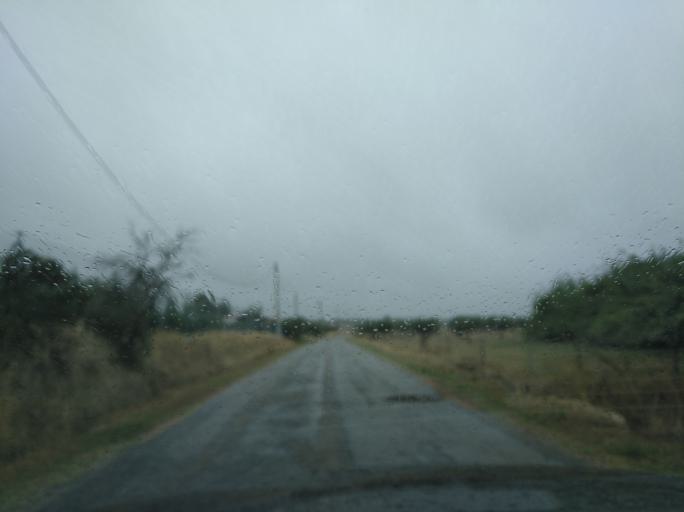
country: PT
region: Portalegre
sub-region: Campo Maior
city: Campo Maior
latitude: 38.9781
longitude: -7.0693
